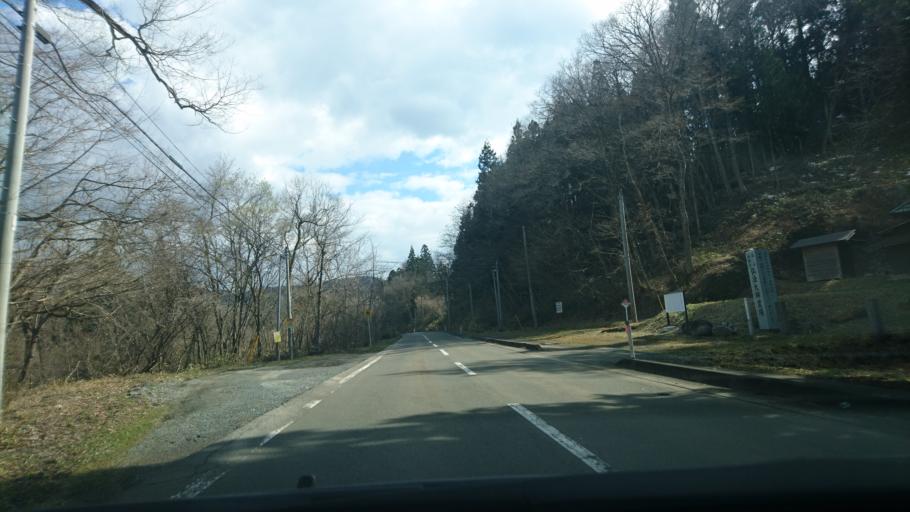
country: JP
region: Iwate
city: Hanamaki
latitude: 39.3394
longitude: 141.2376
